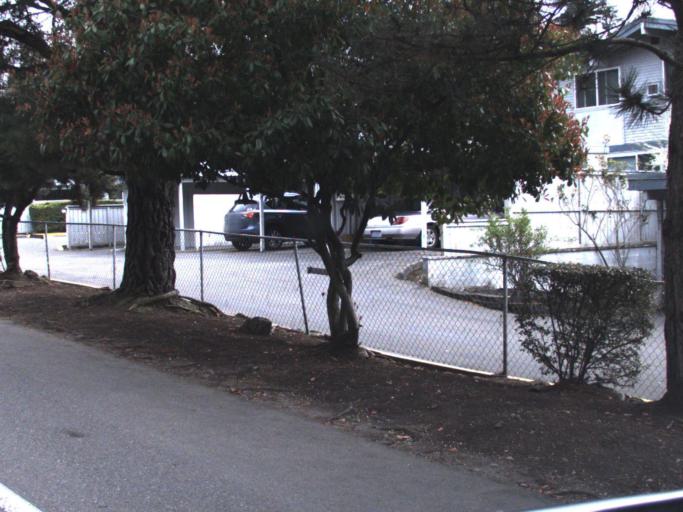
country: US
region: Washington
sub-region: King County
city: Des Moines
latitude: 47.3942
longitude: -122.3042
